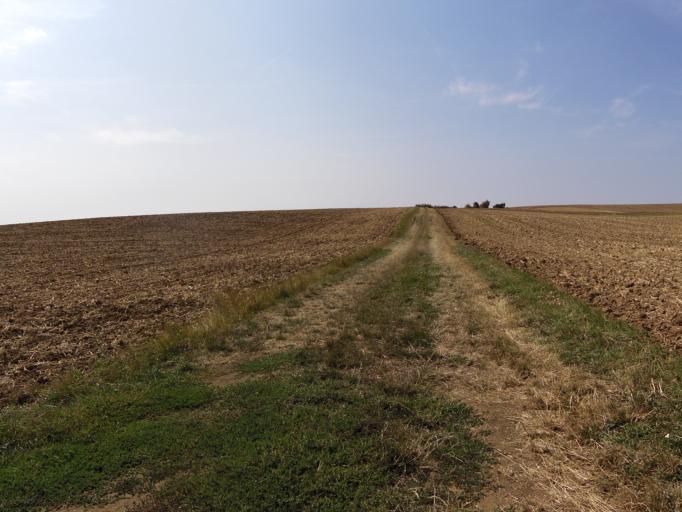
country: DE
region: Bavaria
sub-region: Regierungsbezirk Unterfranken
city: Theilheim
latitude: 49.7680
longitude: 10.0345
